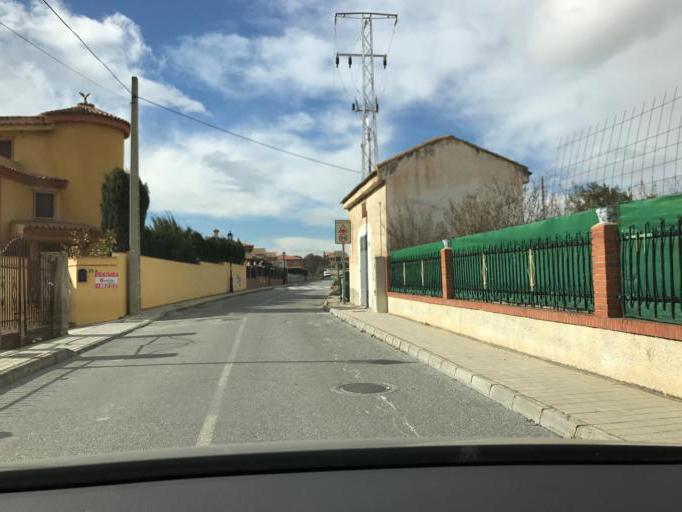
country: ES
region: Andalusia
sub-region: Provincia de Granada
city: Alhendin
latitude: 37.1058
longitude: -3.6653
